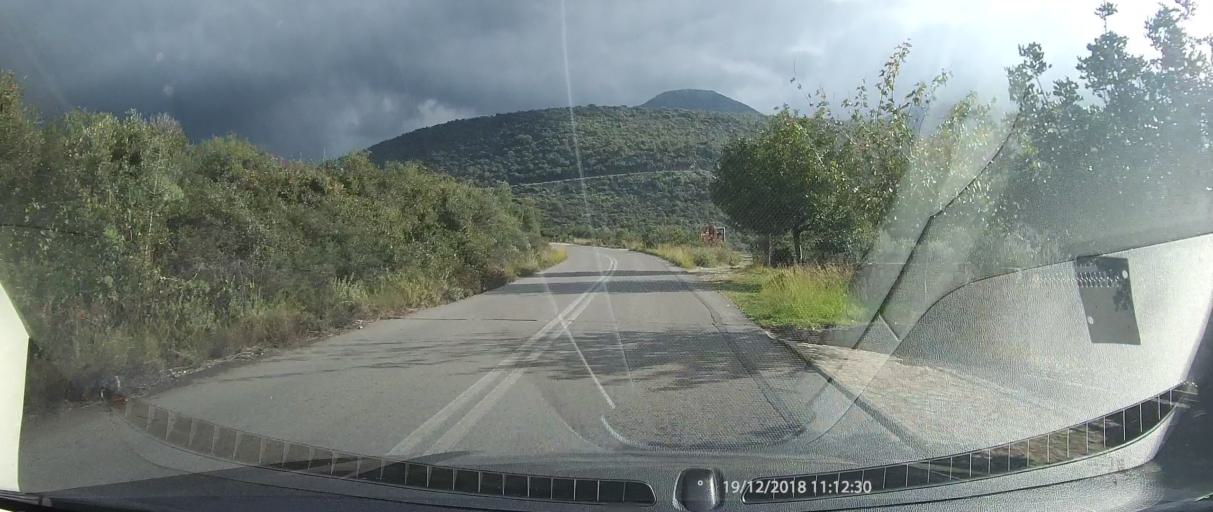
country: GR
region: Peloponnese
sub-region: Nomos Messinias
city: Kardamyli
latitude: 36.8205
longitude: 22.3059
